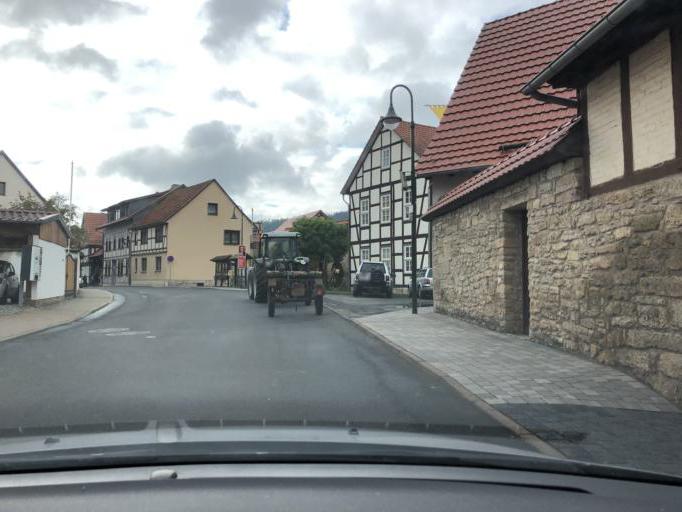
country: DE
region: Thuringia
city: Grossbartloff
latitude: 51.2509
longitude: 10.2115
